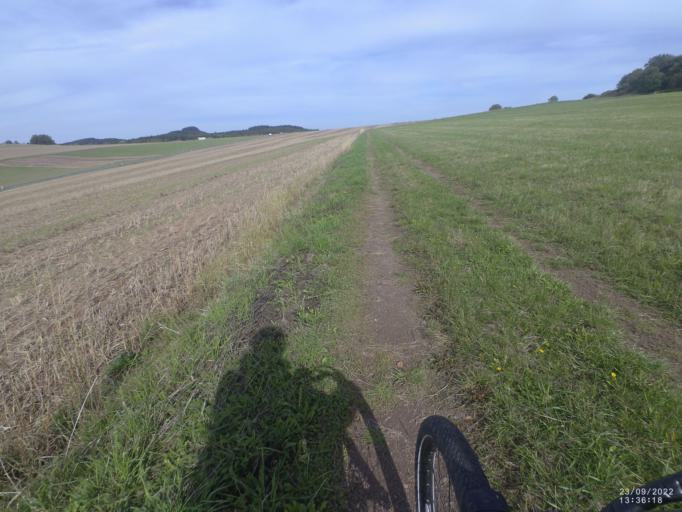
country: DE
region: Rheinland-Pfalz
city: Hinterweiler
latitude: 50.2410
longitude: 6.7628
